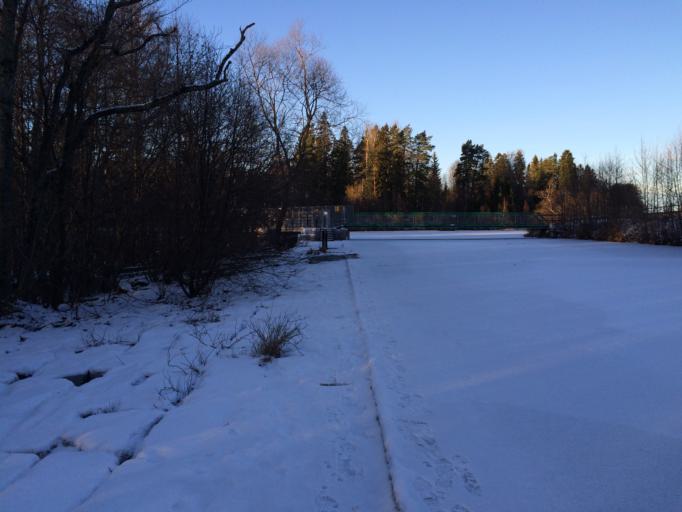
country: SE
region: Vaestmanland
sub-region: Hallstahammars Kommun
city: Hallstahammar
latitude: 59.6288
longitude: 16.2054
